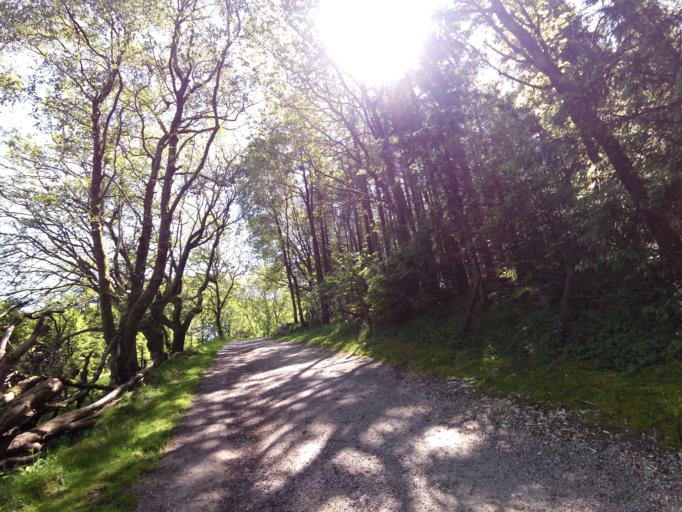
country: NO
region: Rogaland
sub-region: Eigersund
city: Egersund
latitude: 58.5027
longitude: 5.9093
